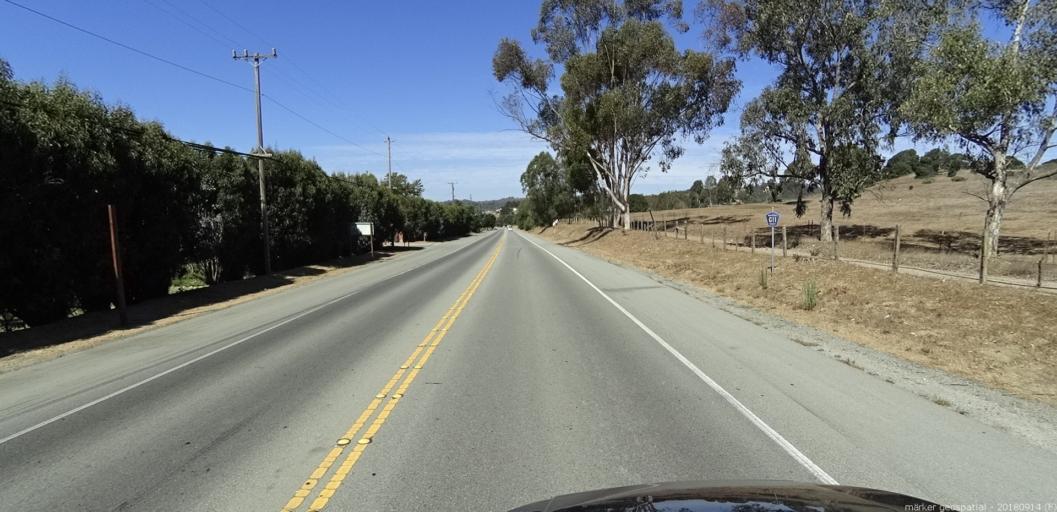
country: US
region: California
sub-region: San Benito County
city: Aromas
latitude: 36.8604
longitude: -121.6540
